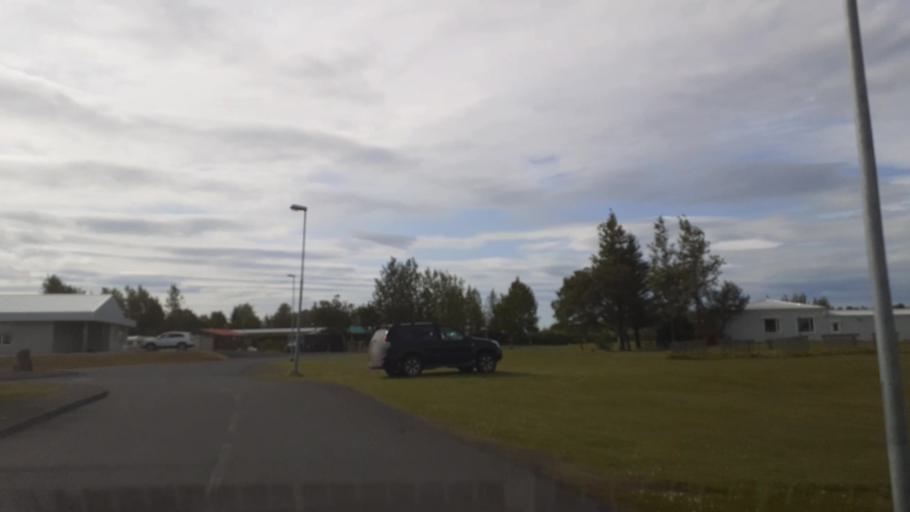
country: IS
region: South
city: Vestmannaeyjar
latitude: 63.8434
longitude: -20.3970
